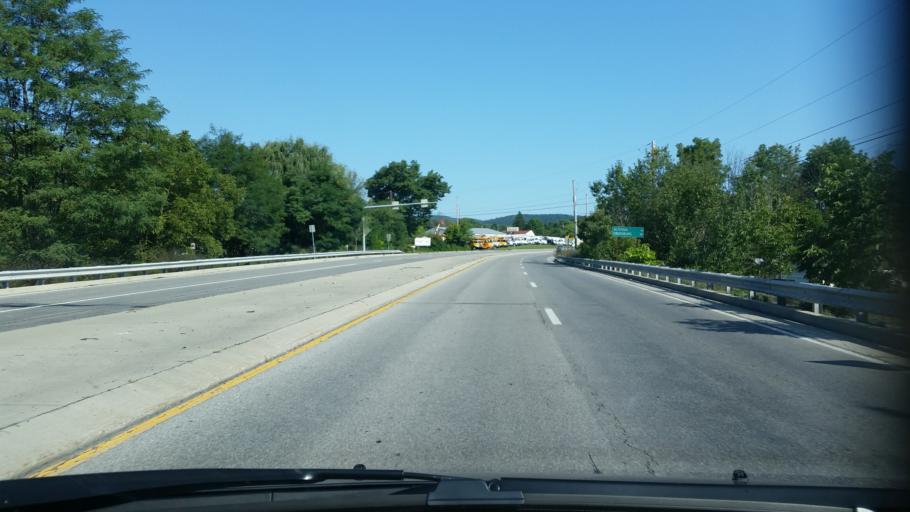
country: US
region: Pennsylvania
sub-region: Blair County
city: Duncansville
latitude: 40.4231
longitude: -78.4406
